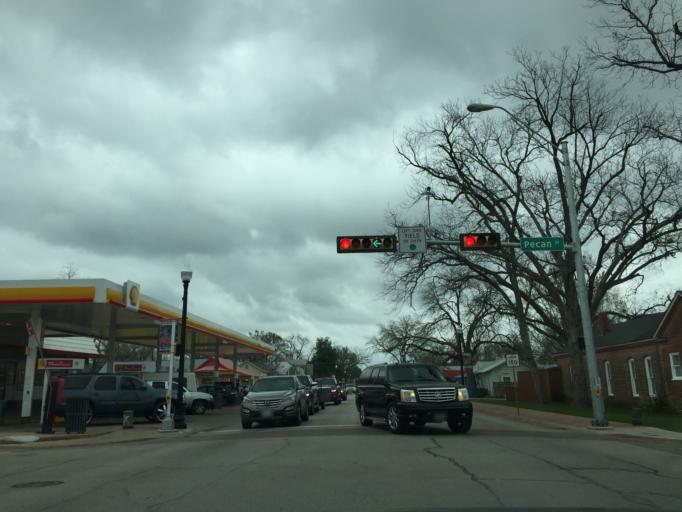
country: US
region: Texas
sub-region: Bastrop County
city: Bastrop
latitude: 30.1106
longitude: -97.3177
